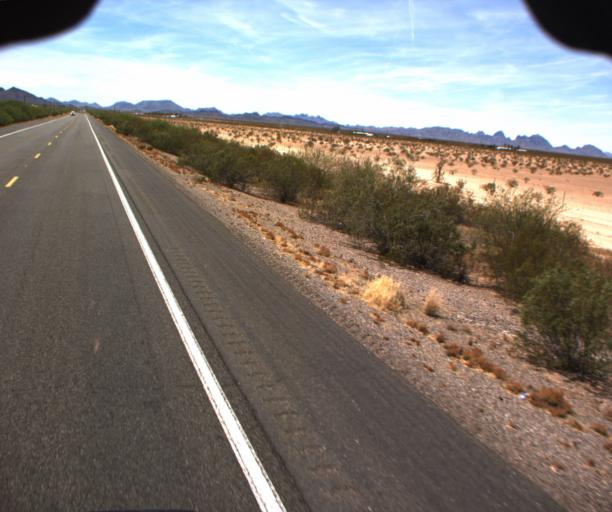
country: US
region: Arizona
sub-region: La Paz County
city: Salome
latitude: 33.7024
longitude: -113.8468
